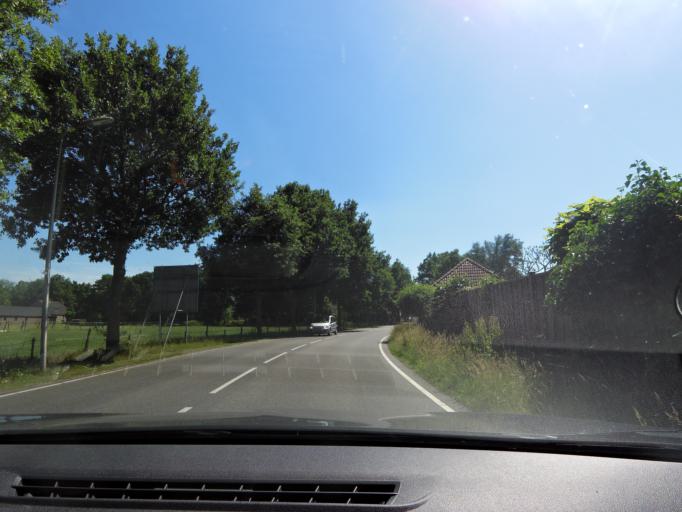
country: NL
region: Gelderland
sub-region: Berkelland
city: Neede
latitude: 52.1348
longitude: 6.6301
